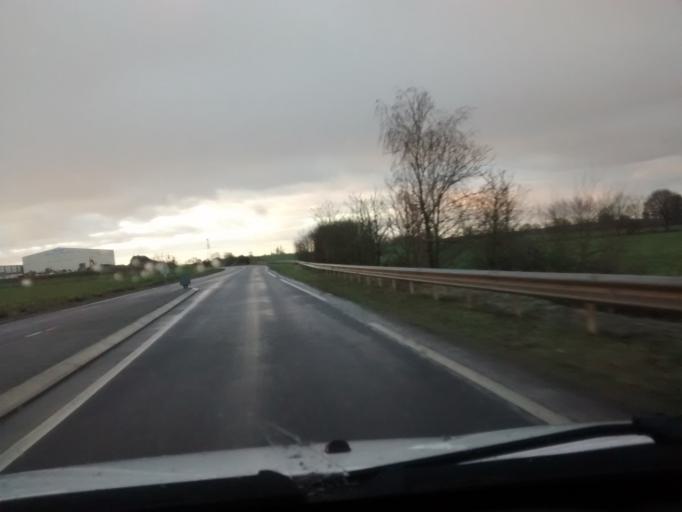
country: FR
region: Brittany
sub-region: Departement d'Ille-et-Vilaine
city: Louvigne-de-Bais
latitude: 48.0422
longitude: -1.3179
